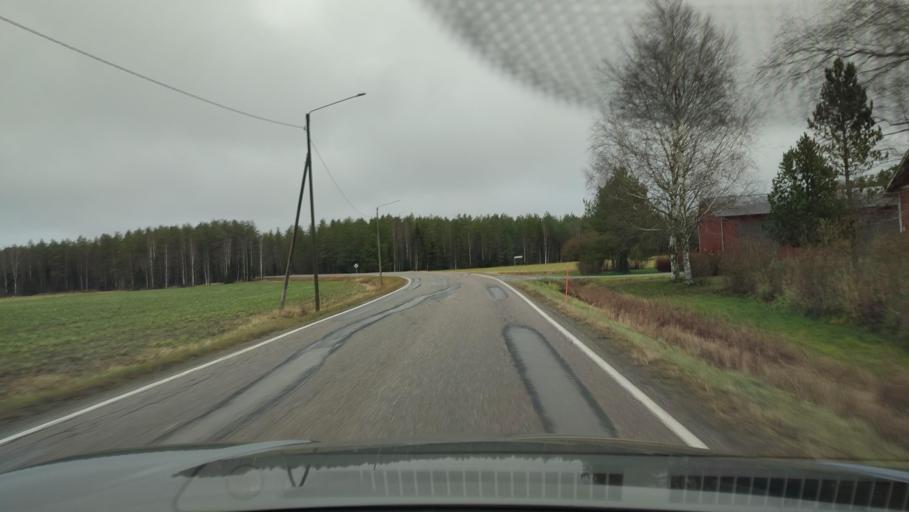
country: FI
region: Southern Ostrobothnia
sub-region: Suupohja
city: Isojoki
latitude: 62.1933
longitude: 21.9865
